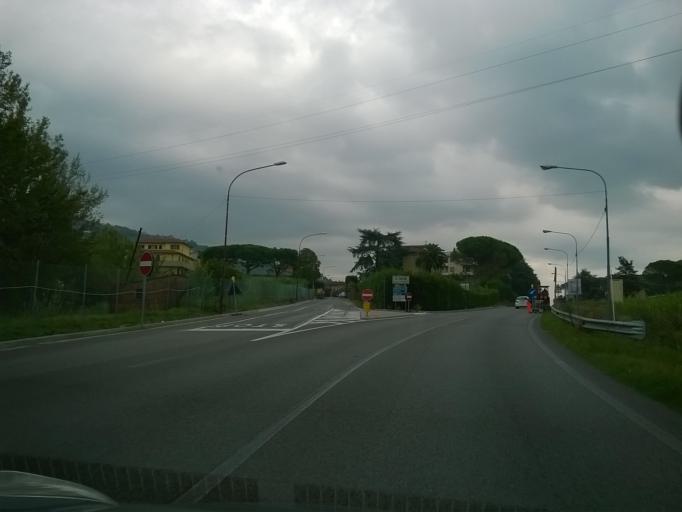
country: IT
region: Tuscany
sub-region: Provincia di Pistoia
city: Santa Lucia
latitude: 43.8798
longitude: 10.7048
